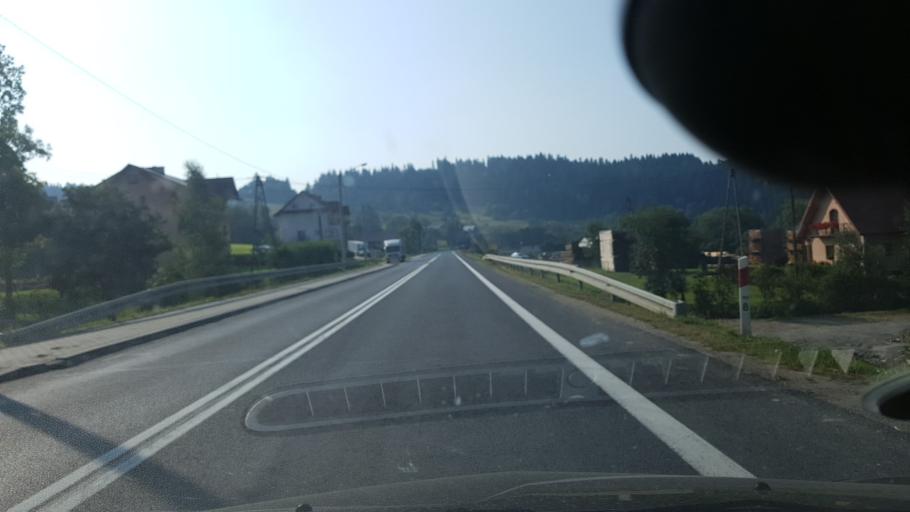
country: PL
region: Lesser Poland Voivodeship
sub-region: Powiat nowotarski
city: Podwilk
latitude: 49.5191
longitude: 19.7207
